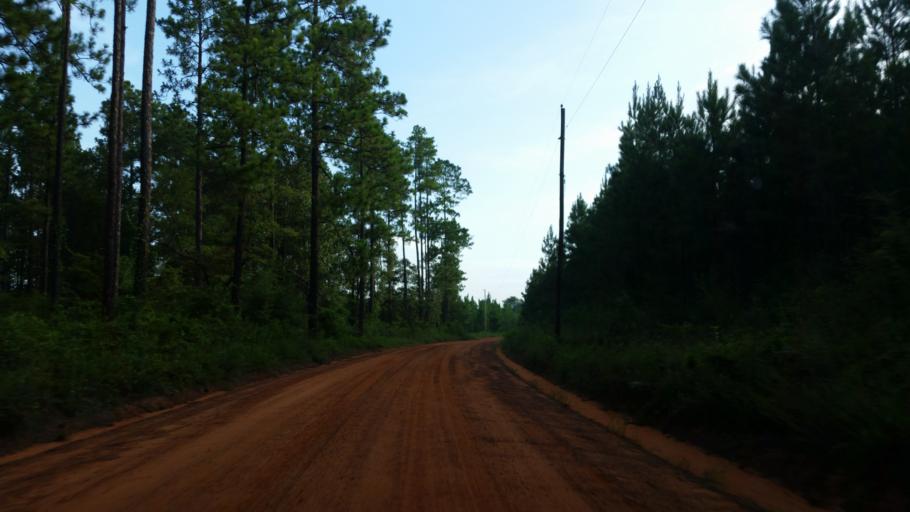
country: US
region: Alabama
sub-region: Escambia County
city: Atmore
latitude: 30.9071
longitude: -87.5832
